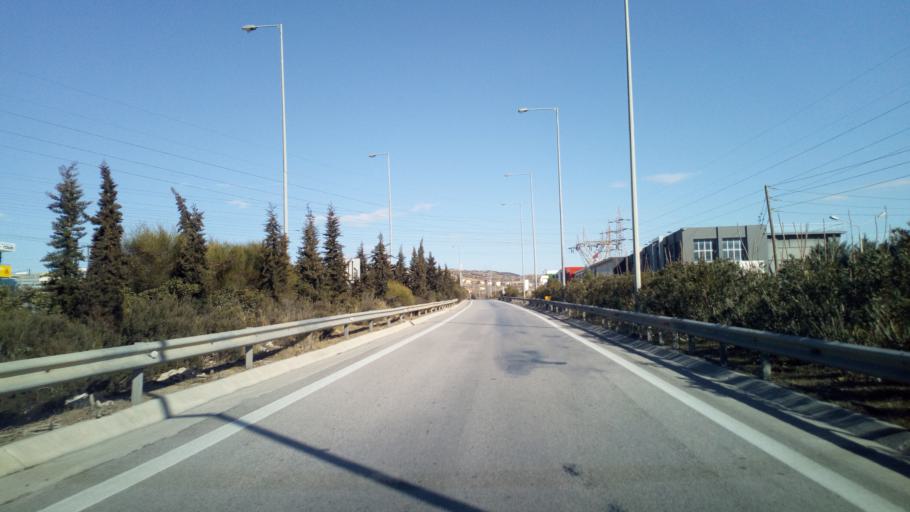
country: GR
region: Central Macedonia
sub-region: Nomos Thessalonikis
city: Efkarpia
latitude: 40.7021
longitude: 22.9514
